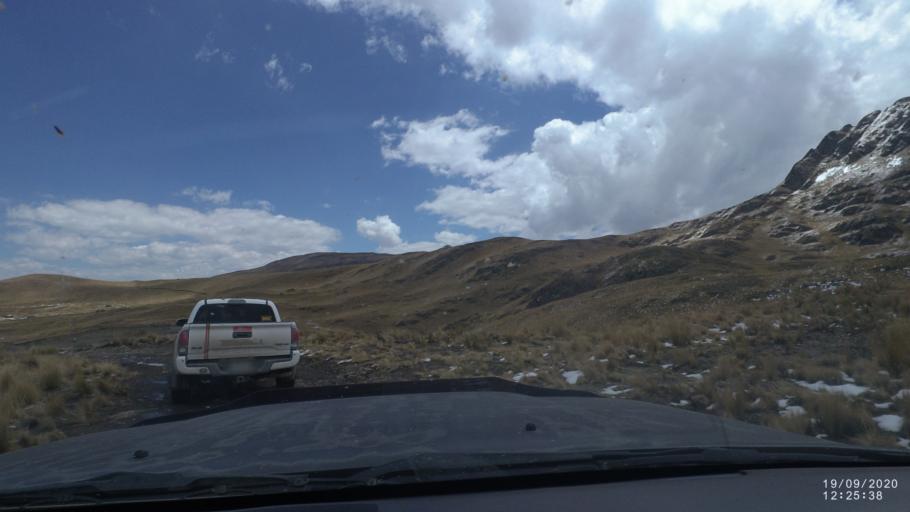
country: BO
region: Cochabamba
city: Cochabamba
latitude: -17.2934
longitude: -66.1112
